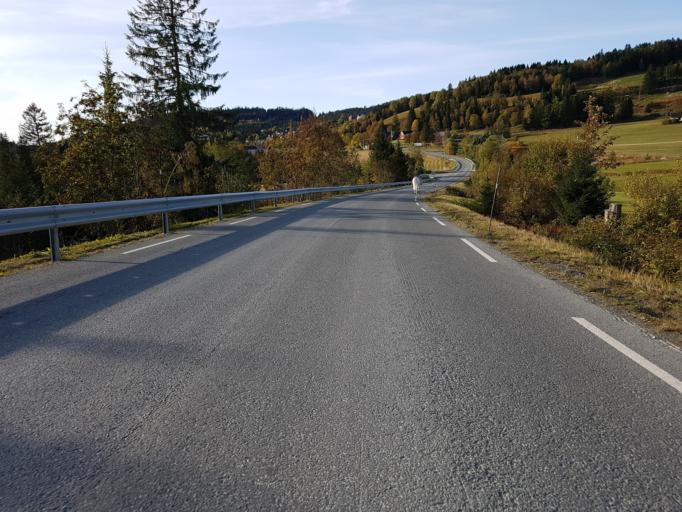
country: NO
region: Sor-Trondelag
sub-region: Klaebu
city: Klaebu
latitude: 63.3478
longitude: 10.5053
